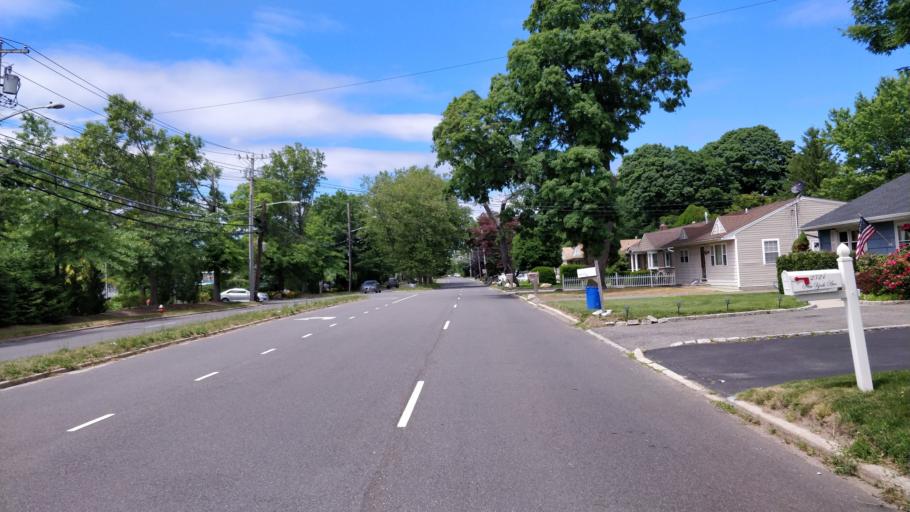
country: US
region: New York
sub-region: Suffolk County
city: South Huntington
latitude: 40.8195
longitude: -73.4074
